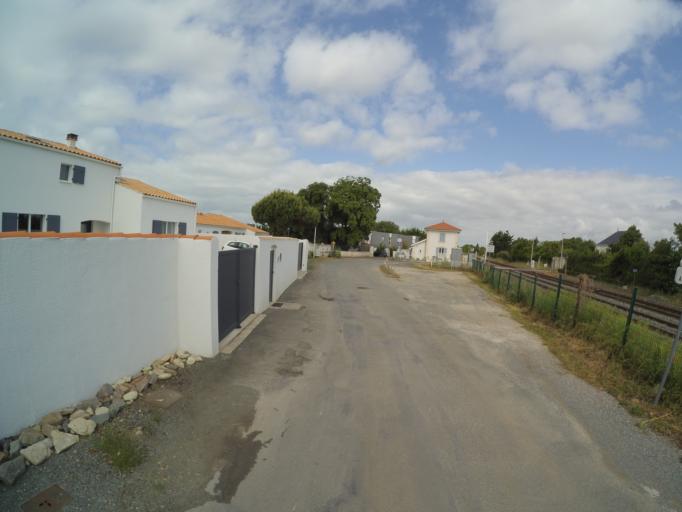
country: FR
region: Poitou-Charentes
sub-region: Departement de la Charente-Maritime
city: Angoulins
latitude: 46.0990
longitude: -1.1078
